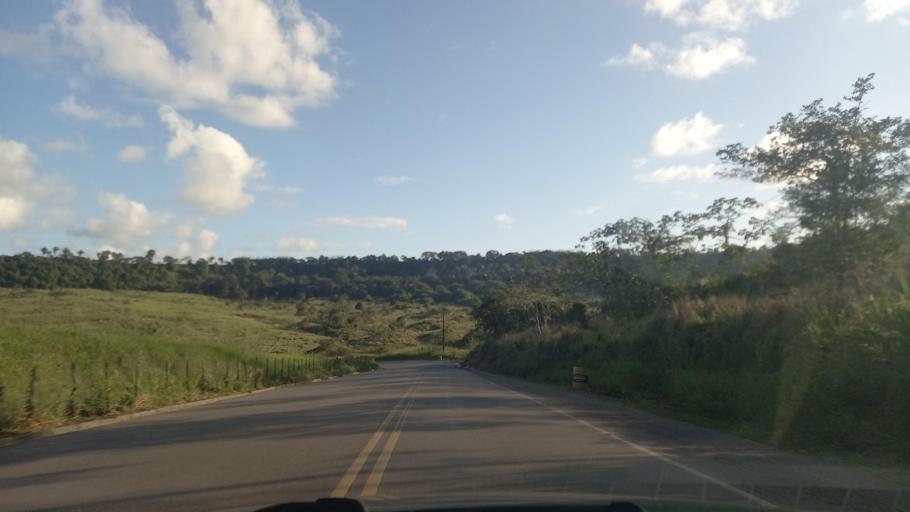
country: BR
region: Alagoas
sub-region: Sao Miguel Dos Campos
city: Sao Miguel dos Campos
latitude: -9.8103
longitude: -36.2211
